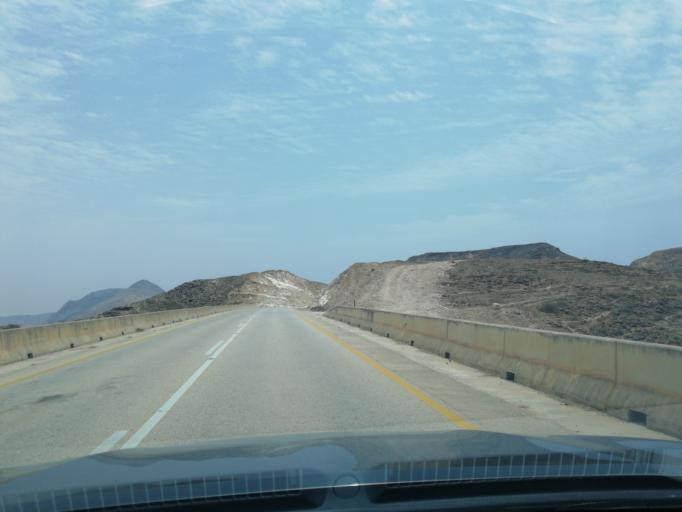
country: OM
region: Zufar
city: Salalah
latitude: 16.8815
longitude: 53.7436
